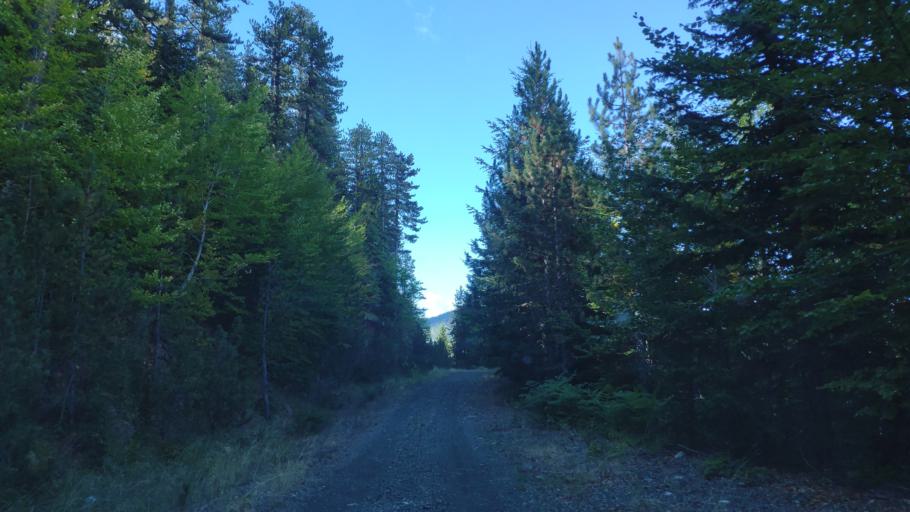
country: GR
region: Epirus
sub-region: Nomos Ioanninon
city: Metsovo
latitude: 39.8906
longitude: 21.2097
